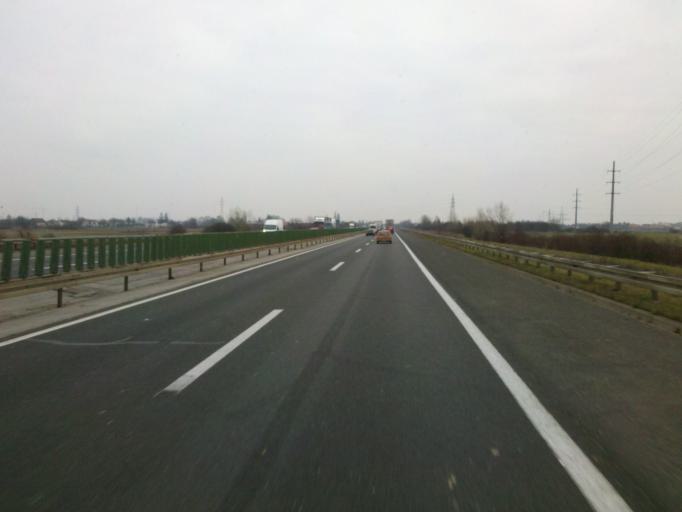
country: HR
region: Grad Zagreb
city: Zadvorsko
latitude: 45.7496
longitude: 15.9430
